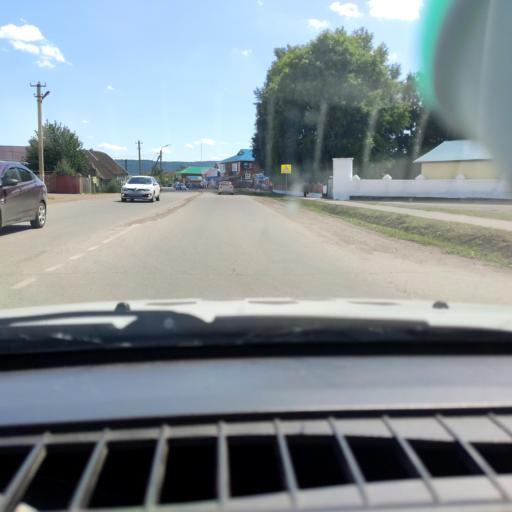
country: RU
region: Bashkortostan
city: Mesyagutovo
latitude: 55.5331
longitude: 58.2481
